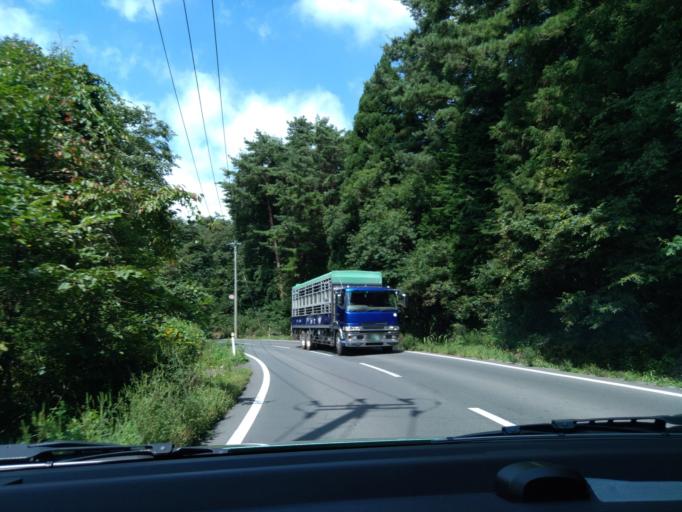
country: JP
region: Iwate
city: Morioka-shi
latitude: 39.5946
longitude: 141.0897
